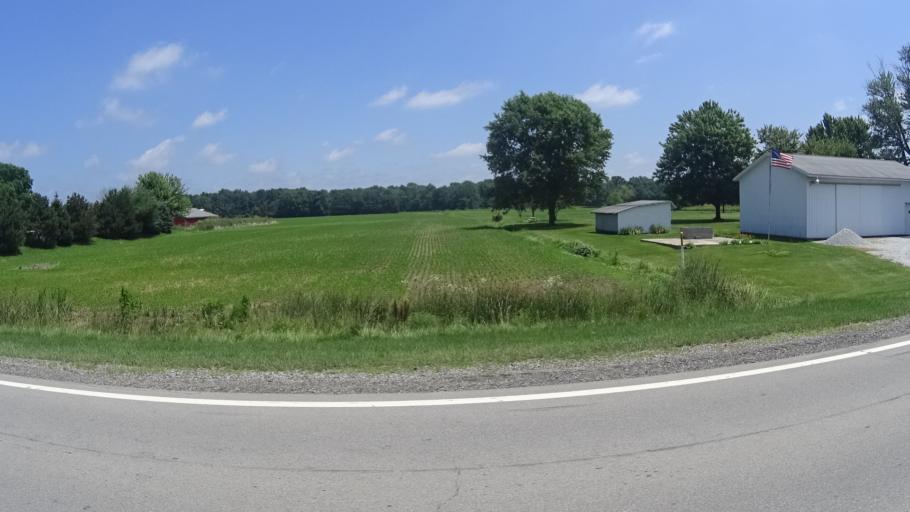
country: US
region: Ohio
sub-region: Lorain County
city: Vermilion
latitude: 41.3483
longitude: -82.3597
